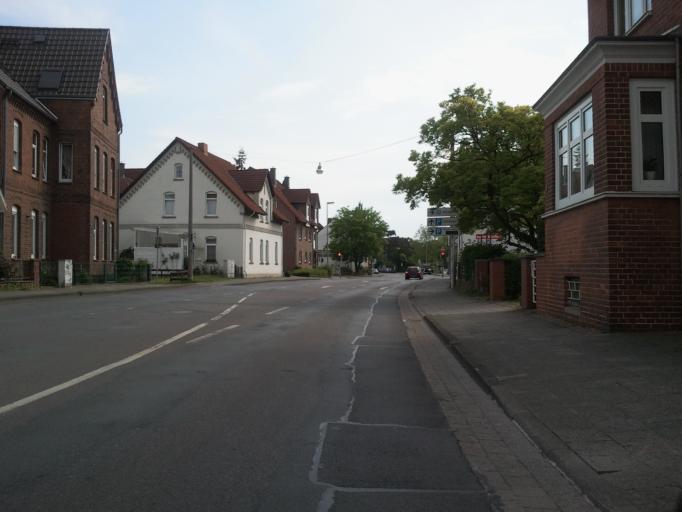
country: DE
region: Lower Saxony
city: Nienburg
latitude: 52.6361
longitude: 9.2090
